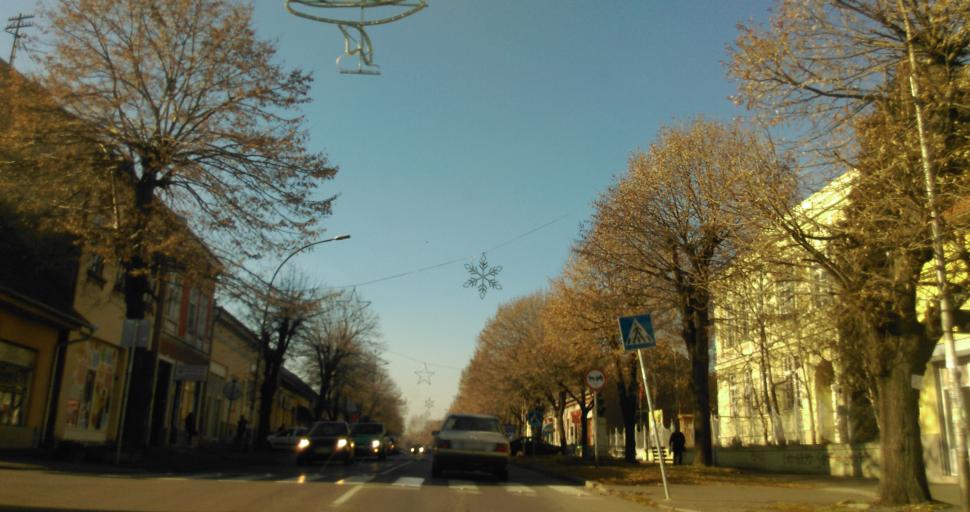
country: RS
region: Autonomna Pokrajina Vojvodina
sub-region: Sremski Okrug
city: Ruma
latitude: 45.0076
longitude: 19.8275
